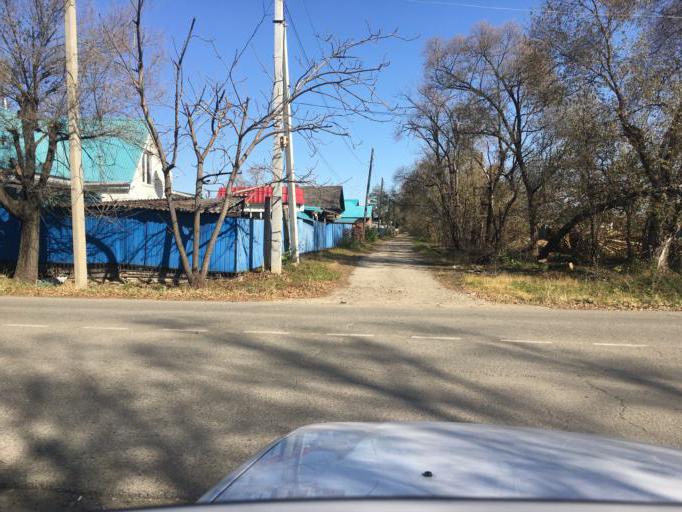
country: RU
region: Primorskiy
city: Dal'nerechensk
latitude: 45.9286
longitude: 133.7385
